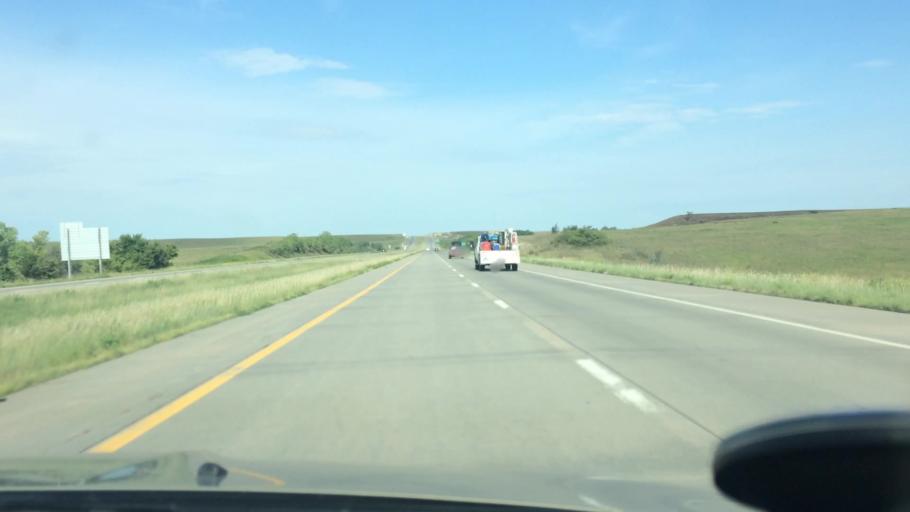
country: US
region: Kansas
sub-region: Riley County
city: Manhattan
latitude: 39.0645
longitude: -96.5628
